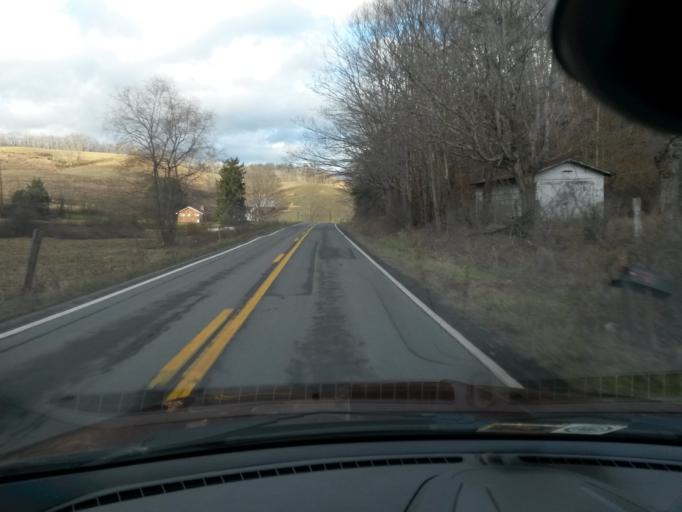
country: US
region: Virginia
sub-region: Giles County
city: Pembroke
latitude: 37.4648
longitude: -80.6604
